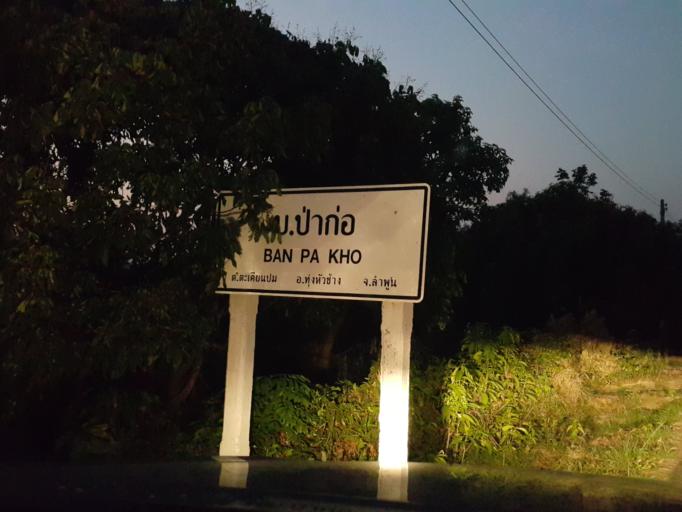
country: TH
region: Lamphun
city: Thung Hua Chang
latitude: 18.1212
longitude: 99.0143
